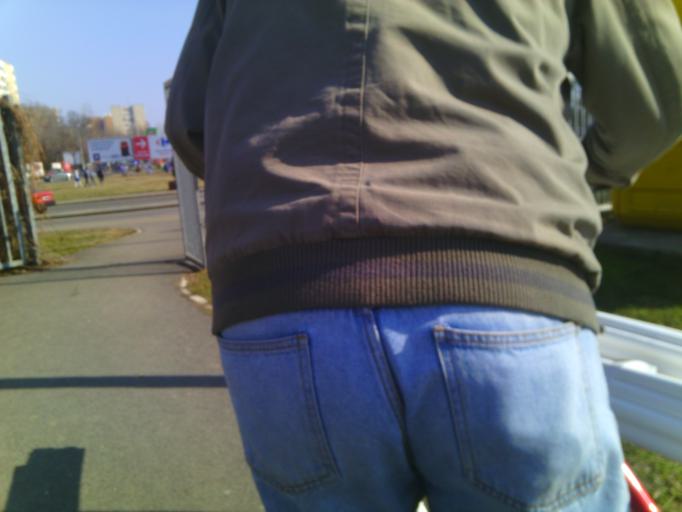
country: RO
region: Ilfov
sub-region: Comuna Popesti-Leordeni
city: Popesti-Leordeni
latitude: 44.3754
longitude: 26.1171
